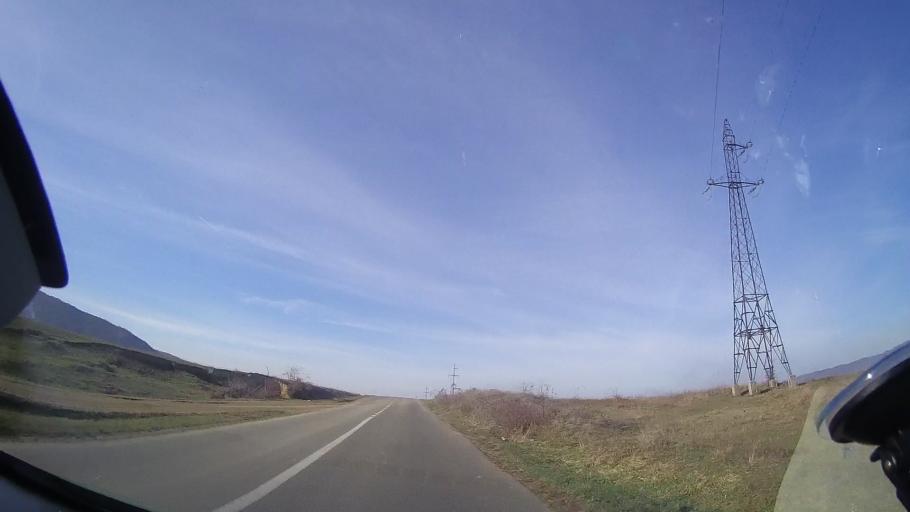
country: RO
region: Bihor
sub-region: Comuna Magesti
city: Magesti
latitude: 47.0208
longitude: 22.4195
